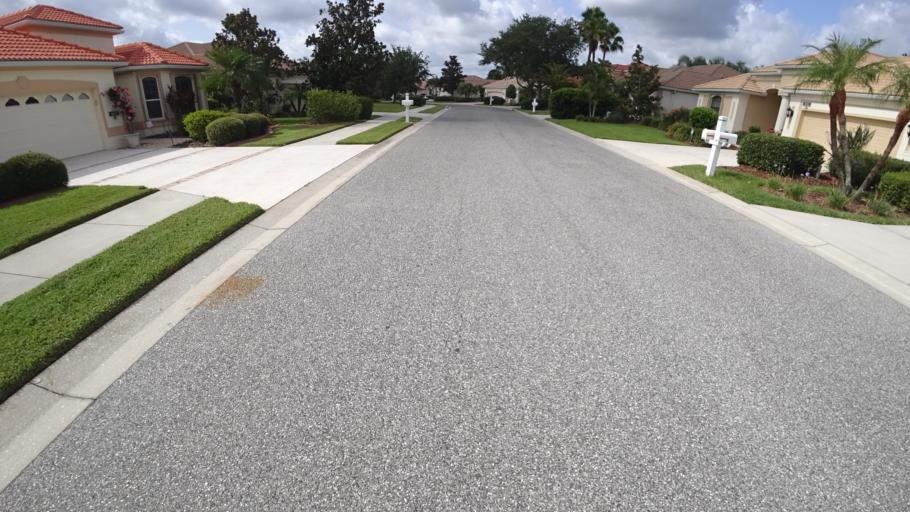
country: US
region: Florida
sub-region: Sarasota County
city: Desoto Lakes
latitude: 27.4384
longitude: -82.4667
